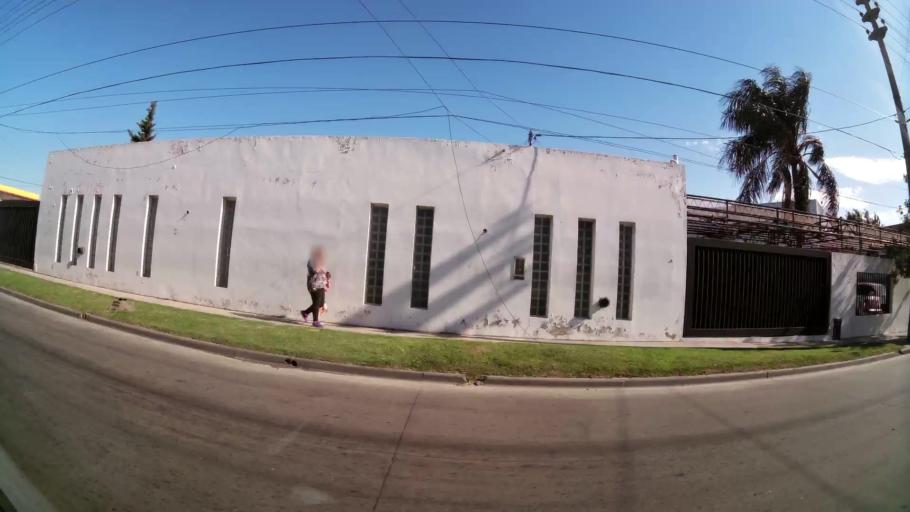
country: AR
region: Buenos Aires
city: Santa Catalina - Dique Lujan
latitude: -34.4785
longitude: -58.6725
